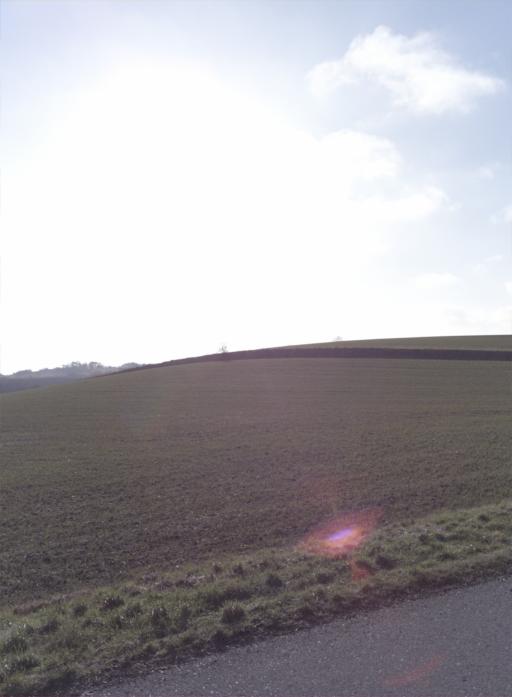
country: DK
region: Zealand
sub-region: Kalundborg Kommune
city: Kalundborg
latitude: 55.6860
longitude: 11.1698
